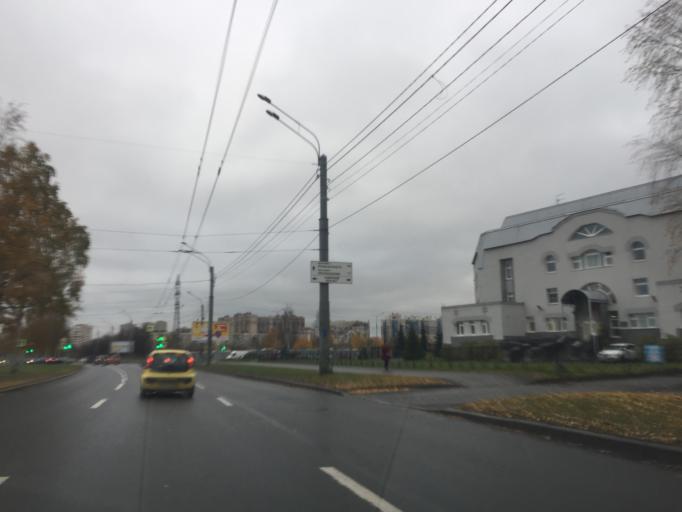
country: RU
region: Leningrad
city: Akademicheskoe
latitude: 60.0264
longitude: 30.3864
